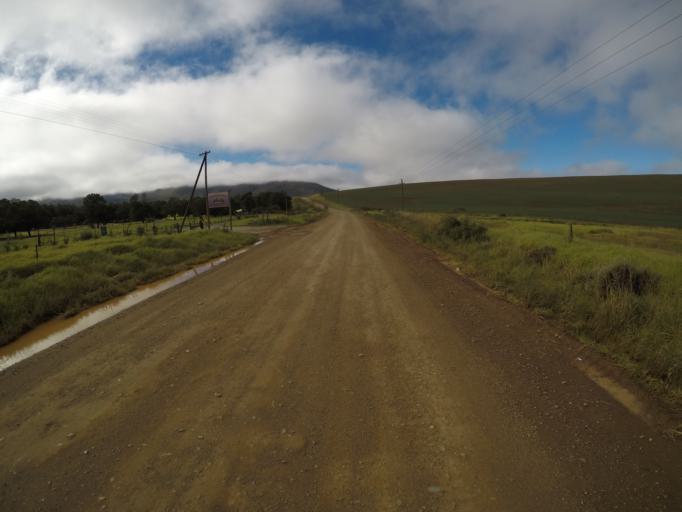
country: ZA
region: Western Cape
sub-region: Cape Winelands District Municipality
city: Ashton
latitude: -34.1307
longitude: 19.8493
